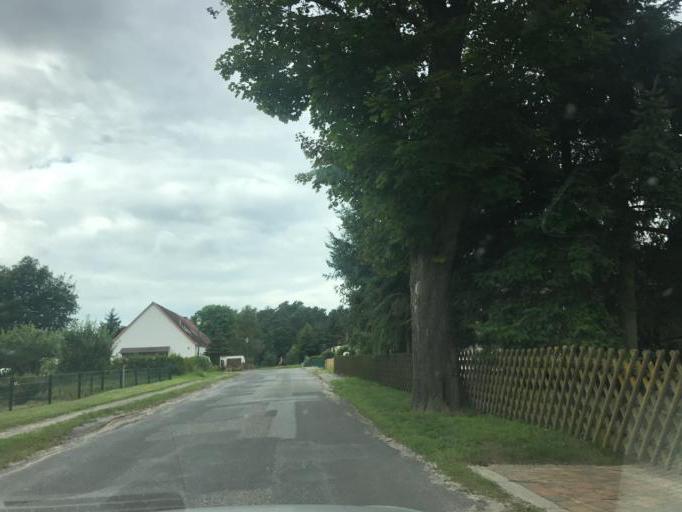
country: DE
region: Mecklenburg-Vorpommern
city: Rechlin
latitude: 53.2327
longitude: 12.7127
